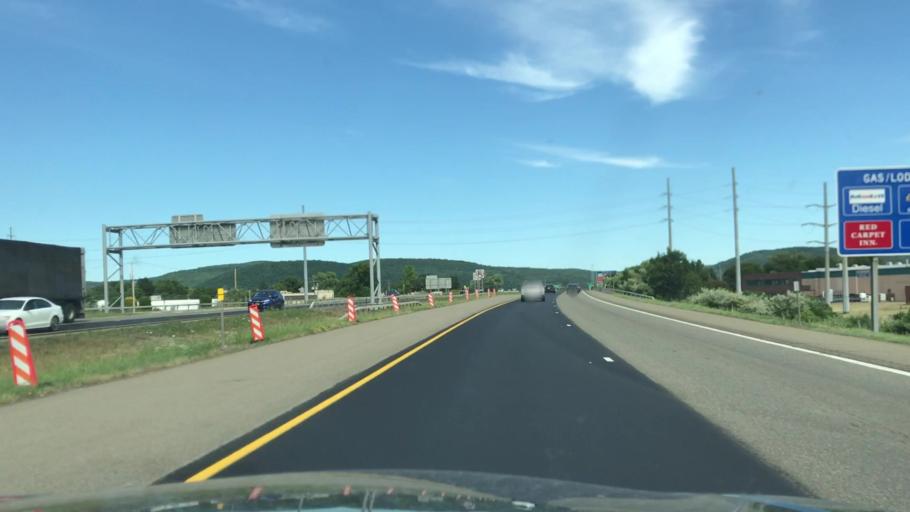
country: US
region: New York
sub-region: Chemung County
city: Horseheads
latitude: 42.1614
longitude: -76.8429
